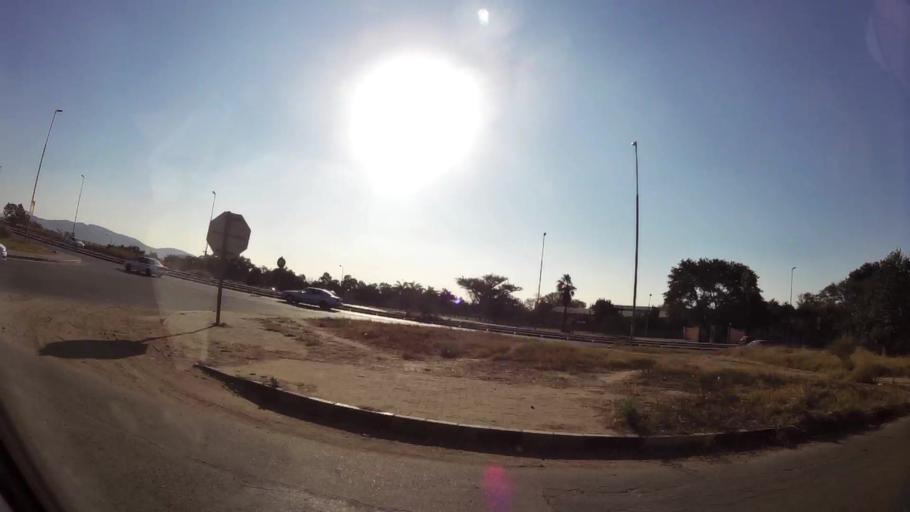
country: ZA
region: North-West
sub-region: Bojanala Platinum District Municipality
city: Rustenburg
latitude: -25.6546
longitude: 27.2459
